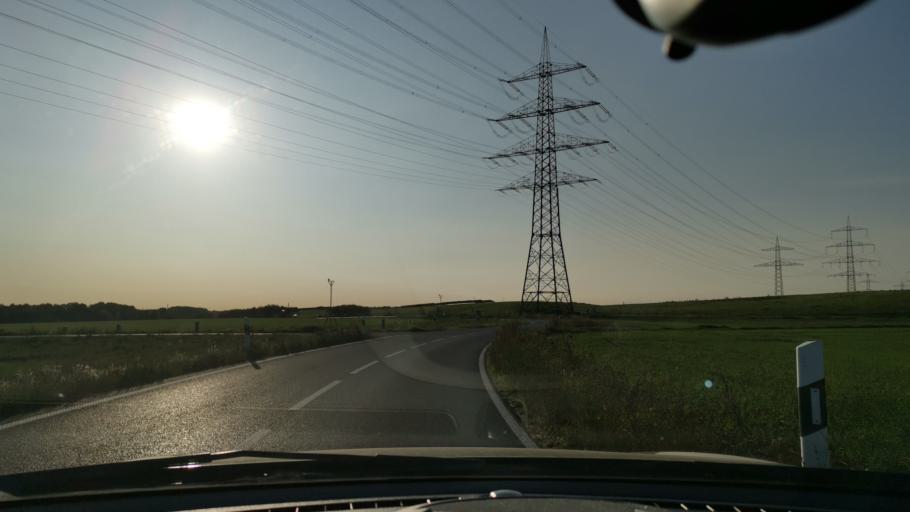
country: DE
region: North Rhine-Westphalia
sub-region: Regierungsbezirk Dusseldorf
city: Rommerskirchen
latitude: 51.0864
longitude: 6.7106
